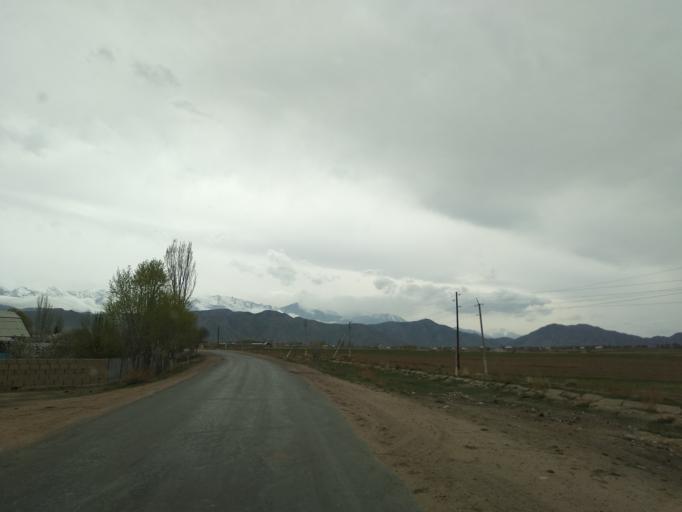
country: KG
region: Ysyk-Koel
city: Bokombayevskoye
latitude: 42.1249
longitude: 76.9896
